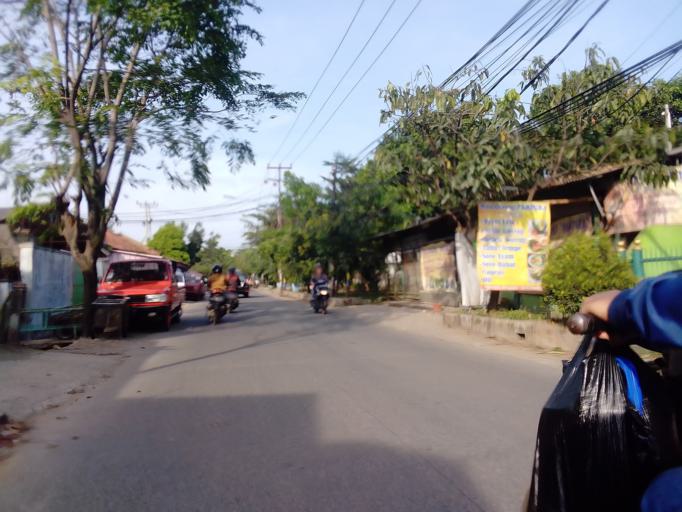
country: ID
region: West Java
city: Cileunyi
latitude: -6.9240
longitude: 107.6981
